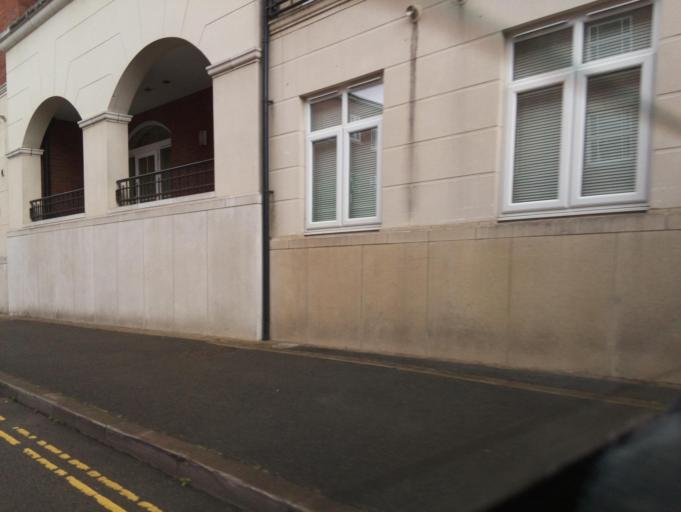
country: GB
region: England
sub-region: Solihull
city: Dickens Heath
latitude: 52.3843
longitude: -1.8369
